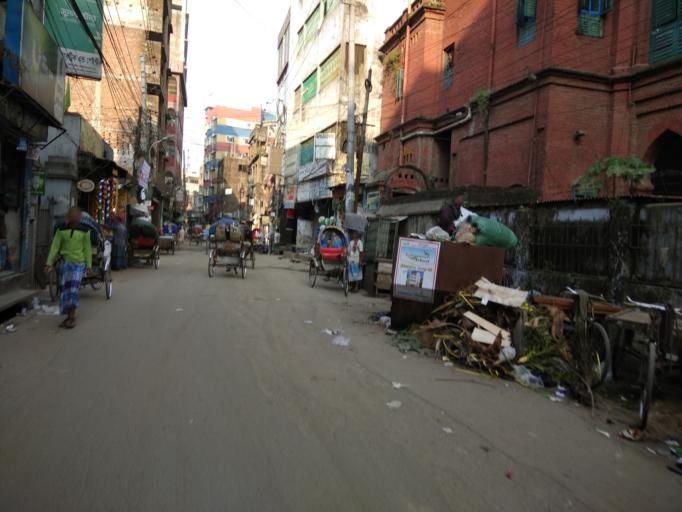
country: BD
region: Dhaka
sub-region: Dhaka
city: Dhaka
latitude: 23.7212
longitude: 90.3991
